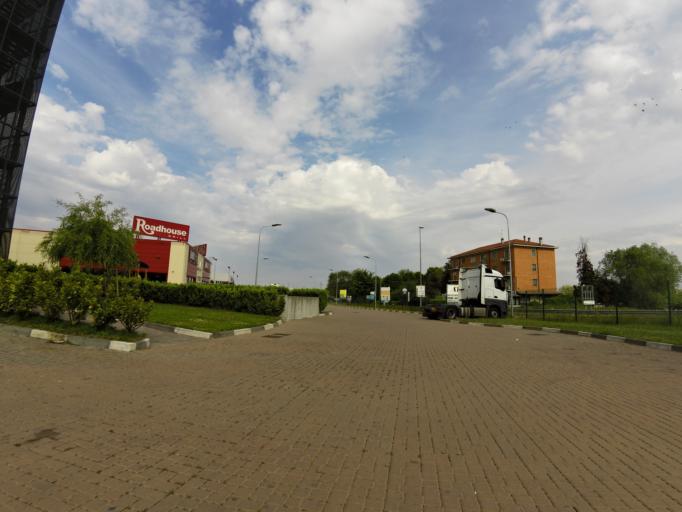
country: IT
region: Lombardy
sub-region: Citta metropolitana di Milano
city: Carpiano
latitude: 45.3483
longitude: 9.2830
